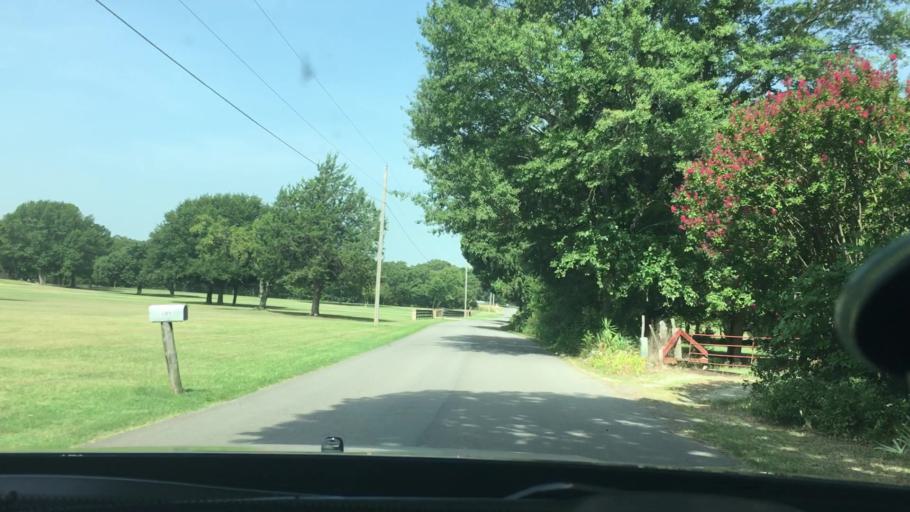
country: US
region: Oklahoma
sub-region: Atoka County
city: Atoka
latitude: 34.3603
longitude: -96.1513
